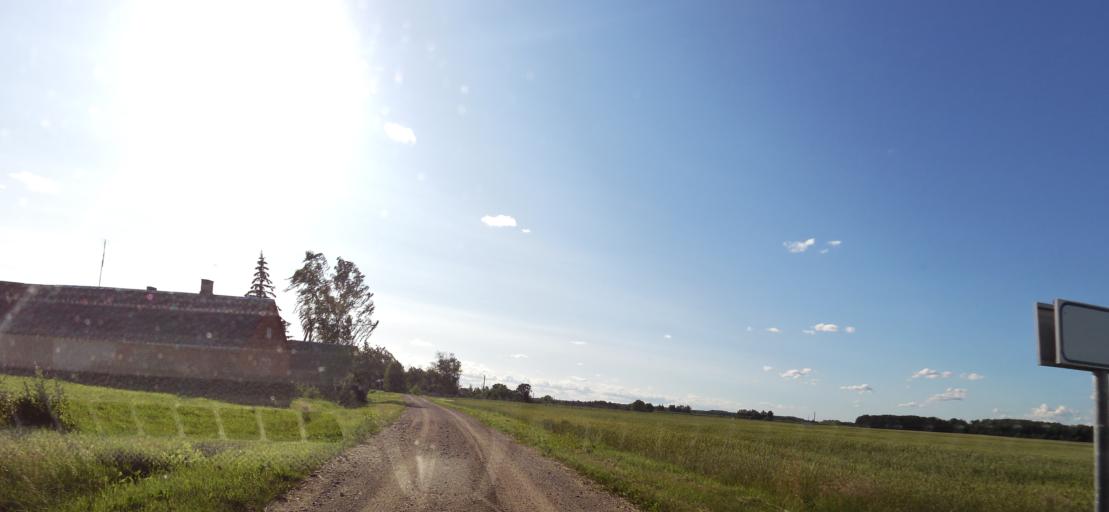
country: LT
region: Panevezys
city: Pasvalys
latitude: 56.1308
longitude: 24.5511
